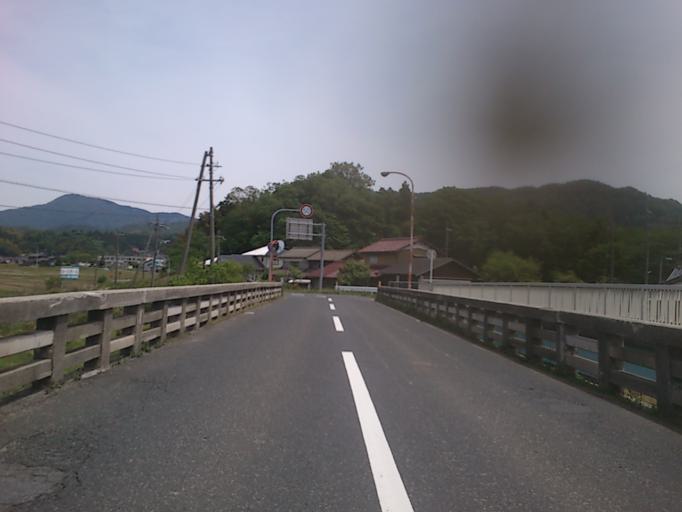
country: JP
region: Kyoto
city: Miyazu
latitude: 35.6401
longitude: 135.0800
